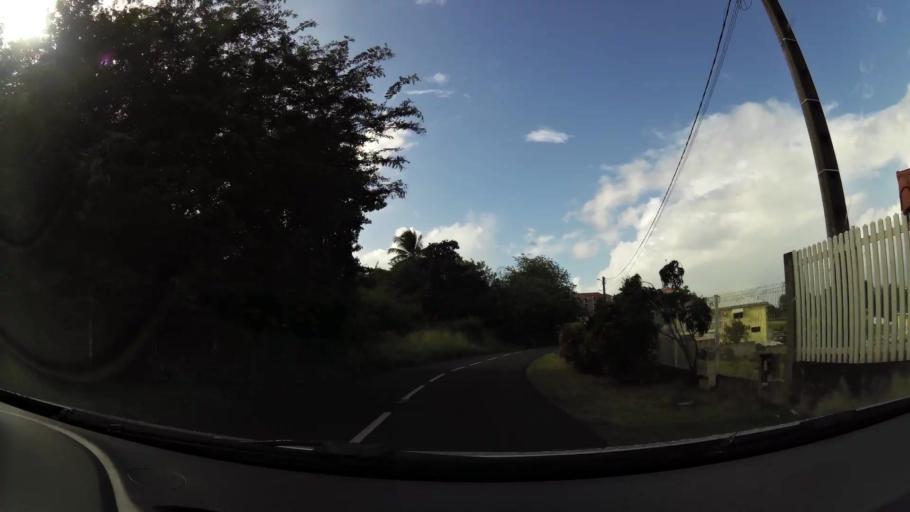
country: MQ
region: Martinique
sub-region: Martinique
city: Saint-Esprit
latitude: 14.5146
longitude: -60.9649
